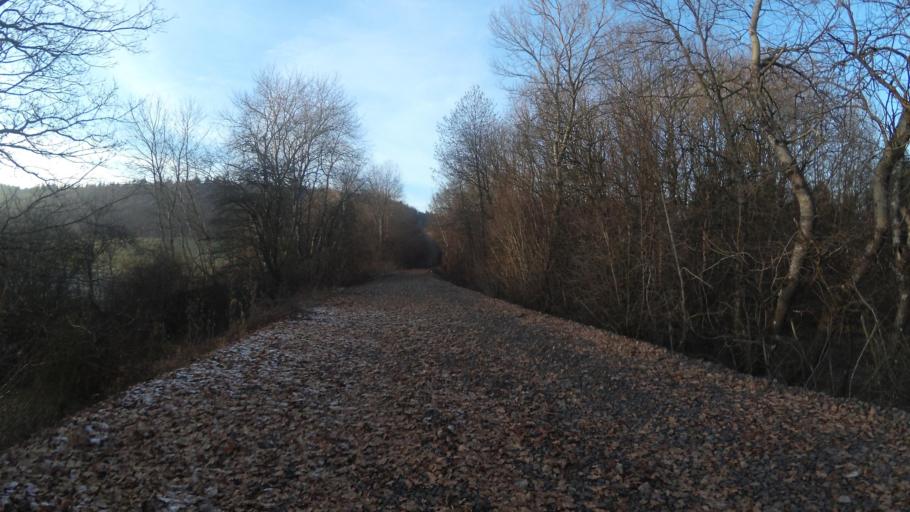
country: DE
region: Saarland
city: Nohfelden
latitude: 49.5698
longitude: 7.1639
